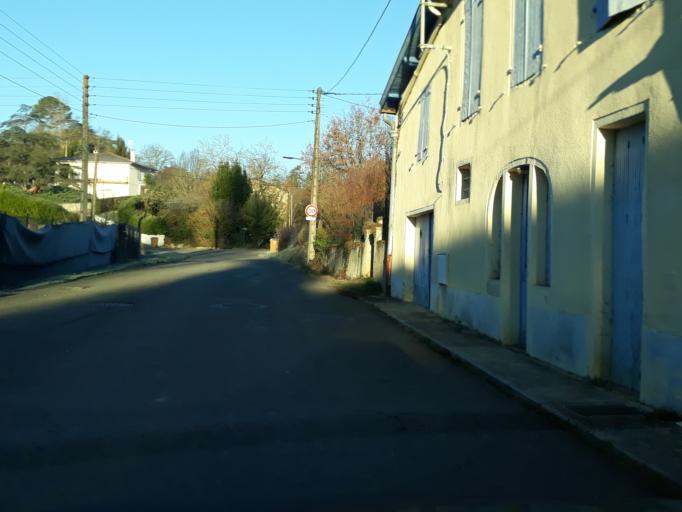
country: FR
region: Midi-Pyrenees
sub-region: Departement du Gers
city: Auch
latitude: 43.6462
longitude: 0.5755
